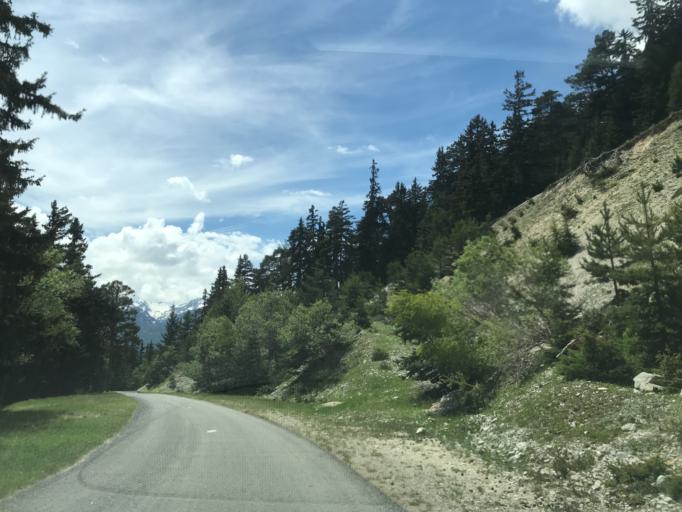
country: FR
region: Rhone-Alpes
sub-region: Departement de la Savoie
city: Modane
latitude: 45.2239
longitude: 6.6652
